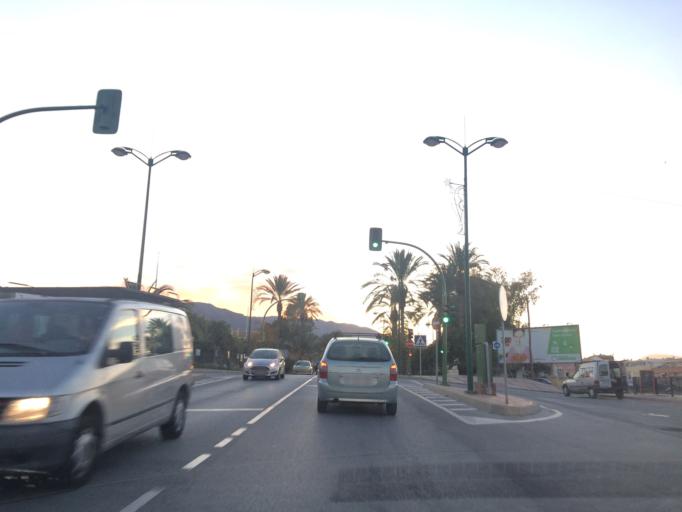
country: ES
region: Andalusia
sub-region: Provincia de Malaga
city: Alhaurin de la Torre
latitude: 36.6610
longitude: -4.5563
